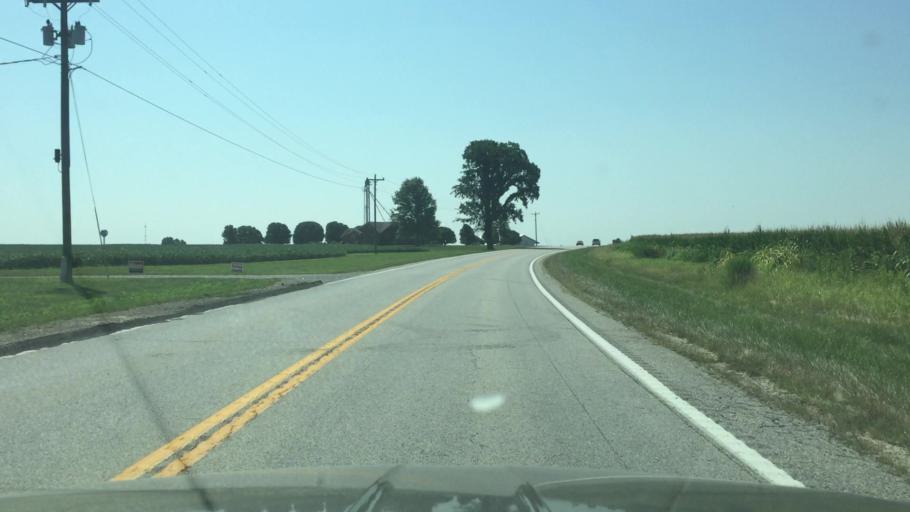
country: US
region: Missouri
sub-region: Moniteau County
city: Tipton
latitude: 38.6605
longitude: -92.8101
